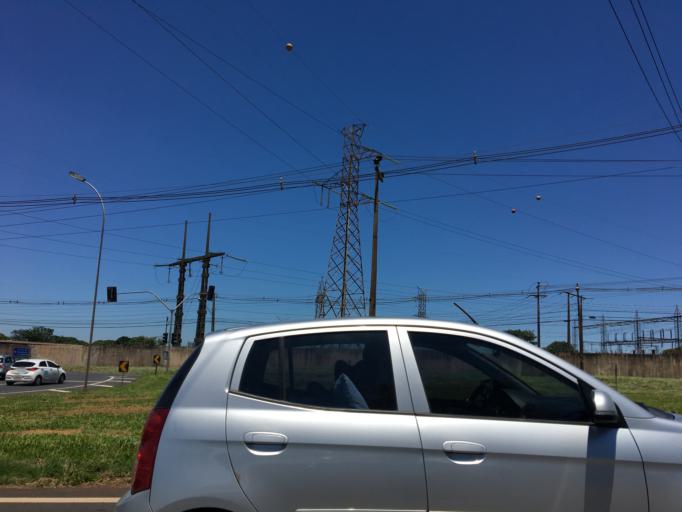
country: BR
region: Parana
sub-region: Maringa
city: Maringa
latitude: -23.4504
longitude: -51.9860
